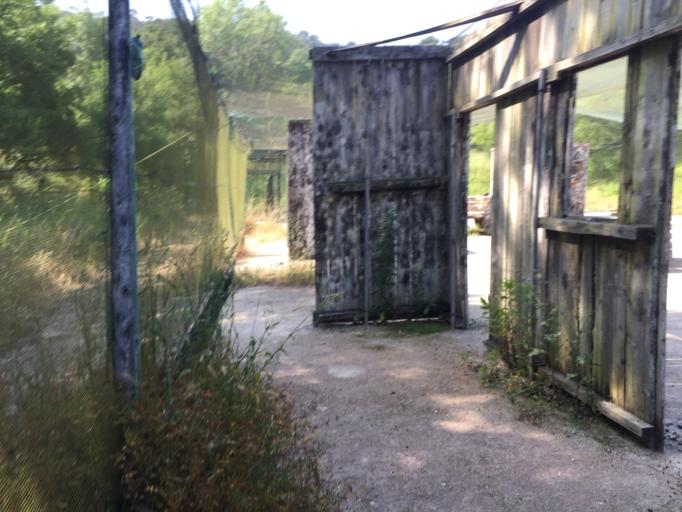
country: PT
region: Lisbon
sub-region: Mafra
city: Milharado
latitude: 38.9022
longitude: -9.1862
